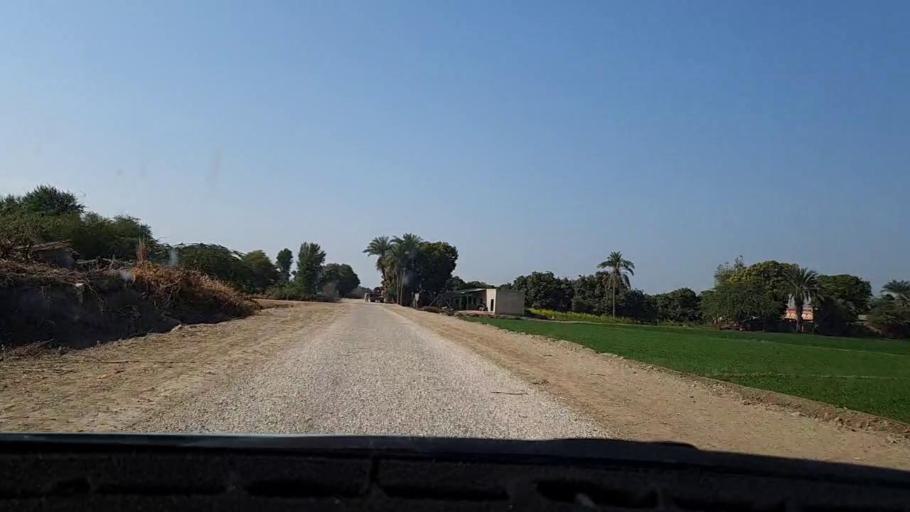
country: PK
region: Sindh
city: Tando Mittha Khan
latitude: 25.8139
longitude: 69.3103
